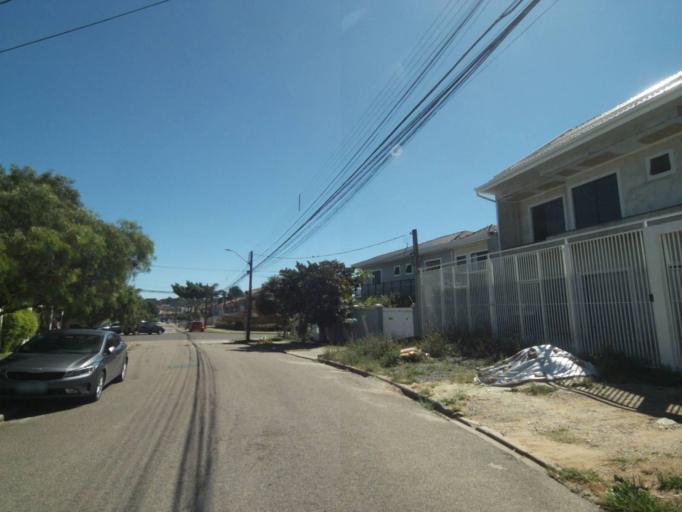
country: BR
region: Parana
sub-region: Curitiba
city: Curitiba
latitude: -25.4819
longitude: -49.3386
